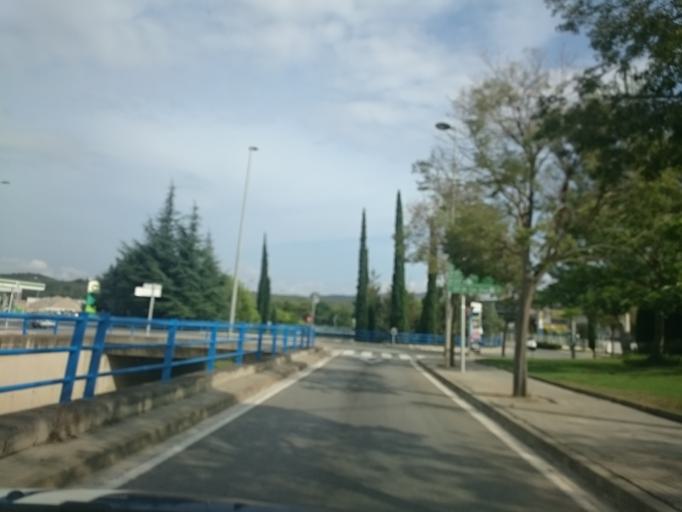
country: ES
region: Catalonia
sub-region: Provincia de Barcelona
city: Sant Cugat del Valles
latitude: 41.4776
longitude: 2.0957
